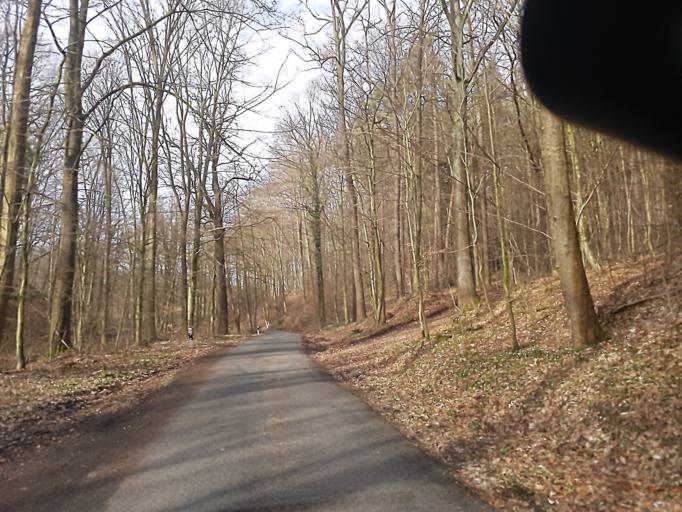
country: DE
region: Saxony
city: Hartha
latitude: 51.1392
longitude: 13.0041
